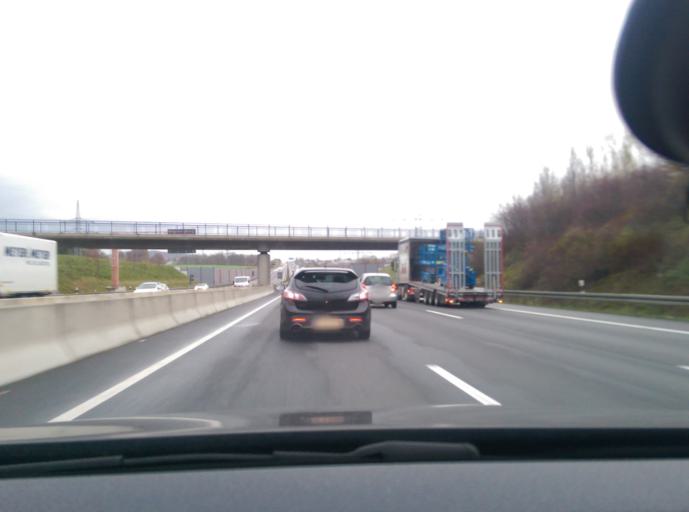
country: DE
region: Lower Saxony
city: Rosdorf
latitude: 51.5299
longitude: 9.8792
